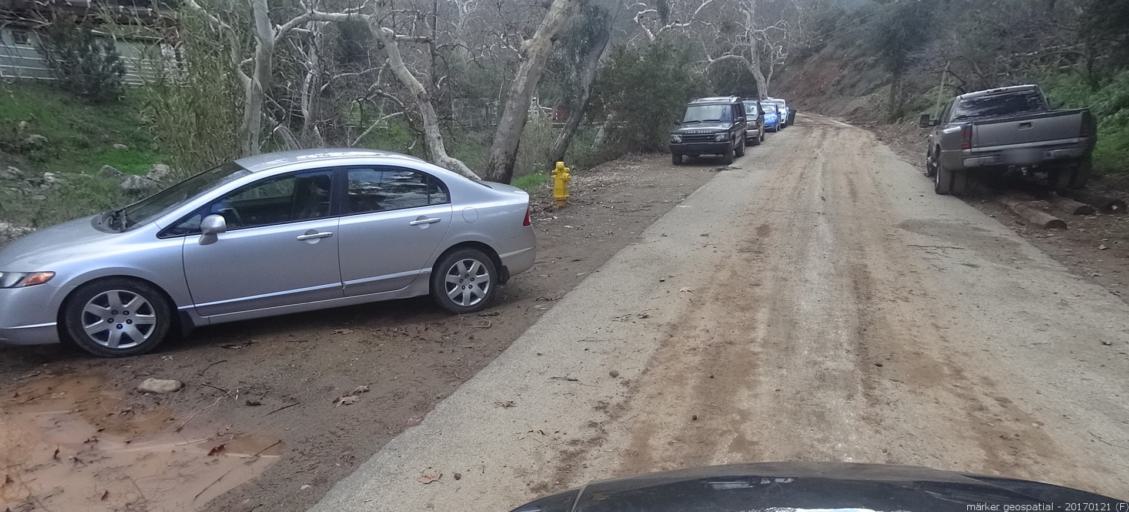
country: US
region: California
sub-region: Orange County
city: Foothill Ranch
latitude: 33.7528
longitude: -117.6384
